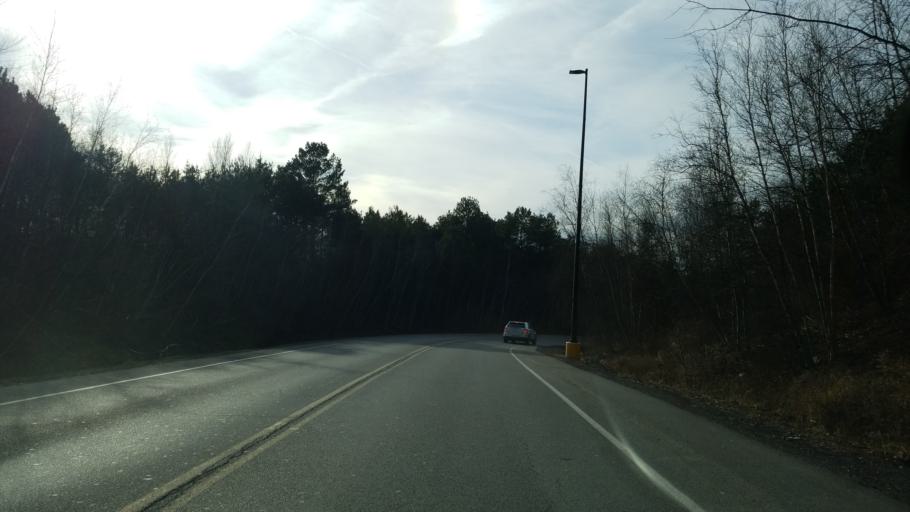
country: US
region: Pennsylvania
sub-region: Clearfield County
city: Clearfield
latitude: 41.0316
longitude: -78.4028
